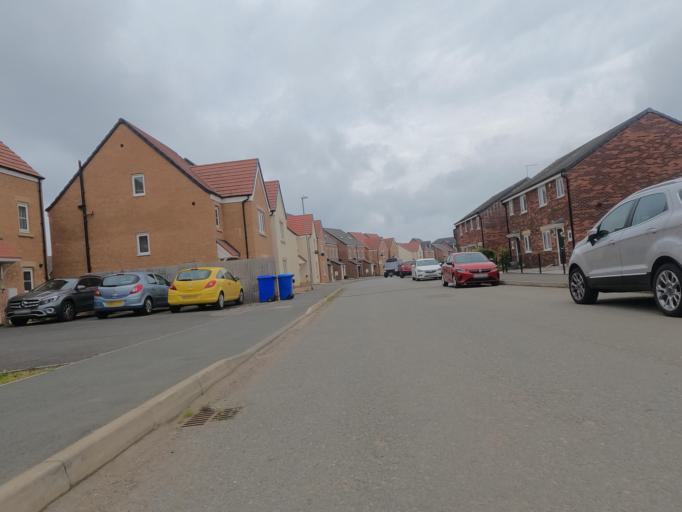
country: GB
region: England
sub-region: Northumberland
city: Blyth
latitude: 55.1205
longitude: -1.5425
